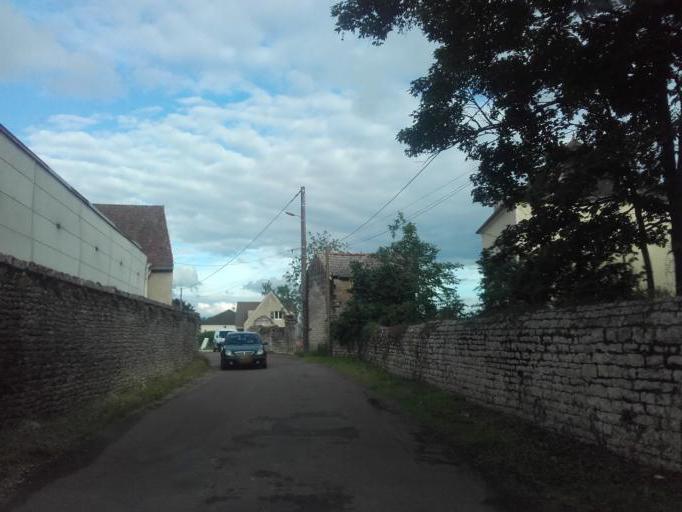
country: FR
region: Bourgogne
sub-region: Departement de Saone-et-Loire
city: Mellecey
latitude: 46.8299
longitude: 4.7386
